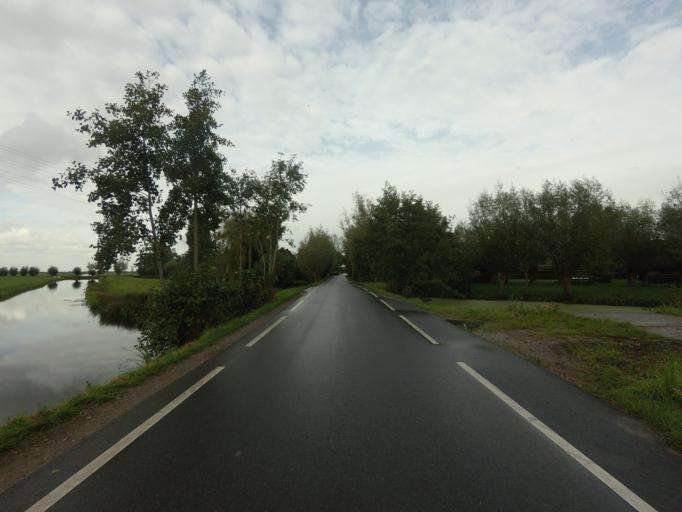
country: NL
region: South Holland
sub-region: Molenwaard
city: Liesveld
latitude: 51.9533
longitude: 4.8226
